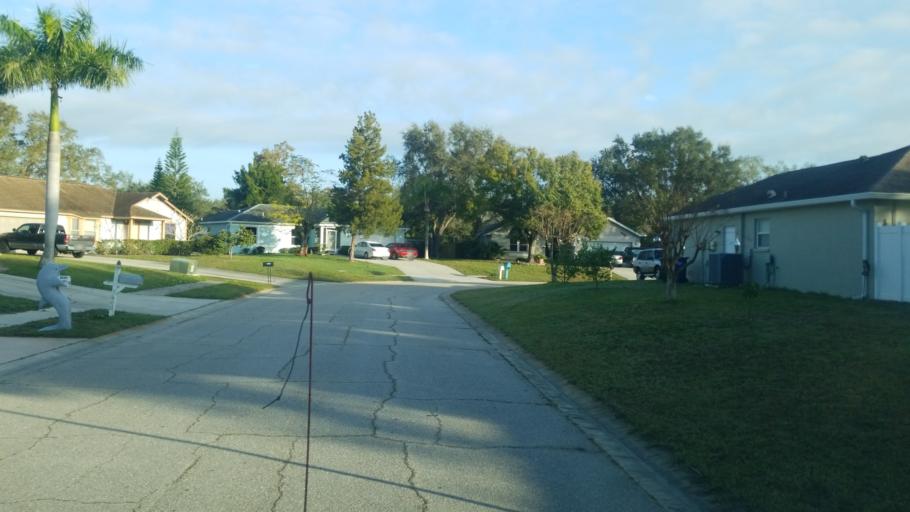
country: US
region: Florida
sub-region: Manatee County
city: Samoset
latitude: 27.4422
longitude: -82.5336
